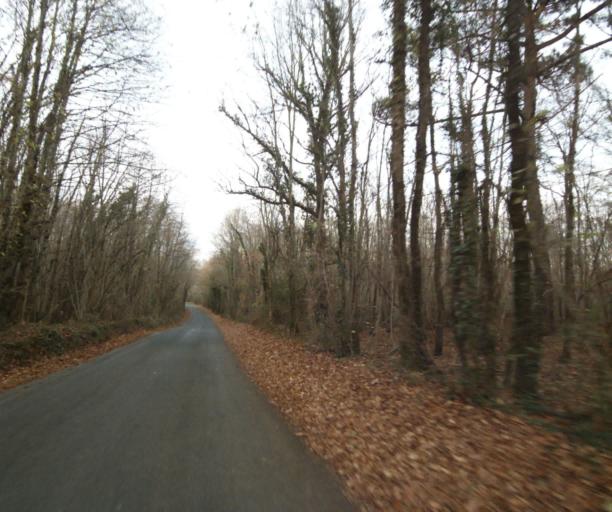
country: FR
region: Poitou-Charentes
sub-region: Departement de la Charente-Maritime
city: Fontcouverte
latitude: 45.7992
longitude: -0.5874
